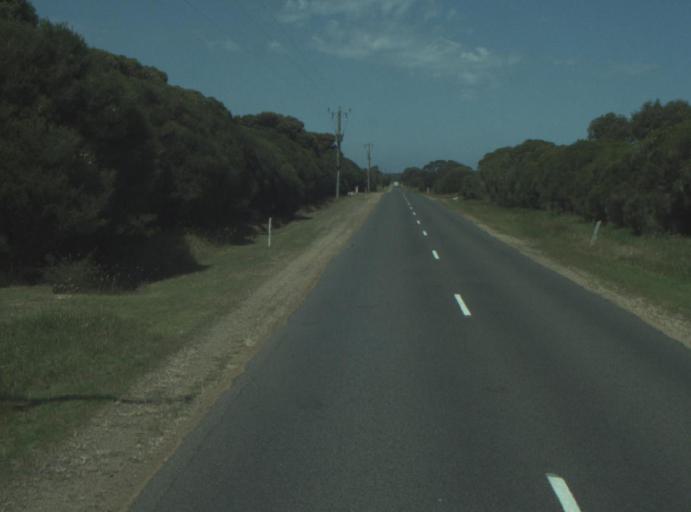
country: AU
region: Victoria
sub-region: Greater Geelong
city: Breakwater
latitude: -38.2768
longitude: 144.4023
